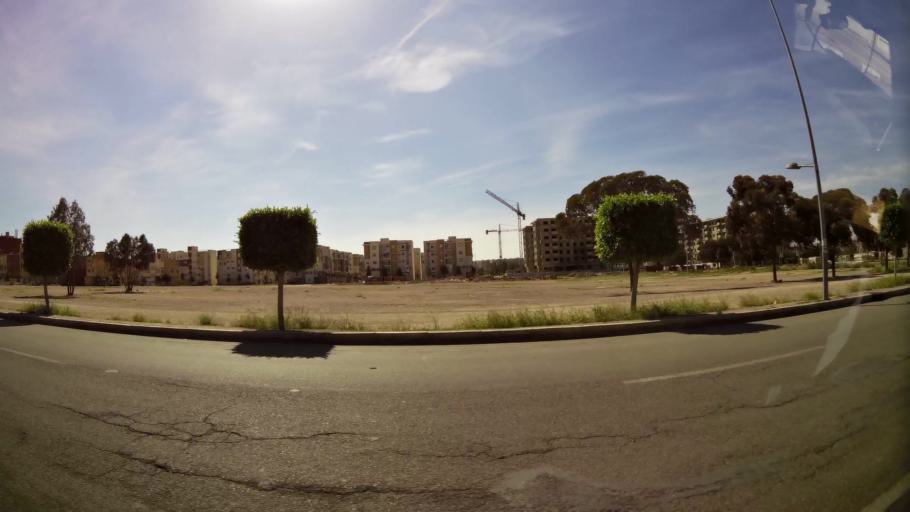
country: MA
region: Oriental
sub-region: Oujda-Angad
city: Oujda
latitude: 34.6626
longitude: -1.9115
